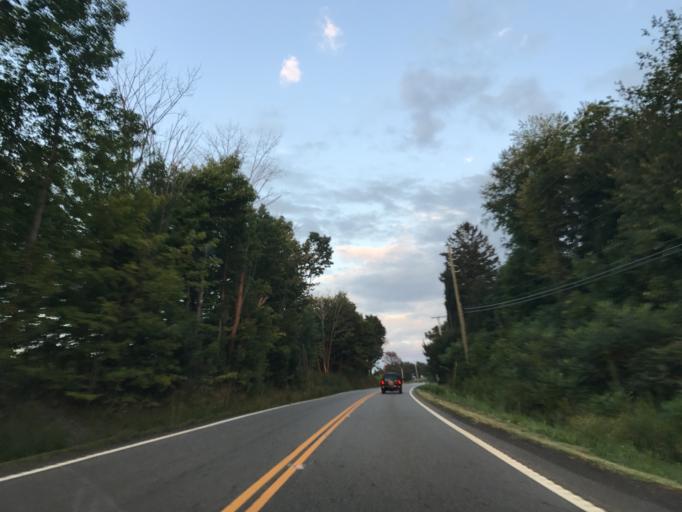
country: US
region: Ohio
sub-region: Columbiana County
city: Lisbon
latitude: 40.7696
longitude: -80.8217
